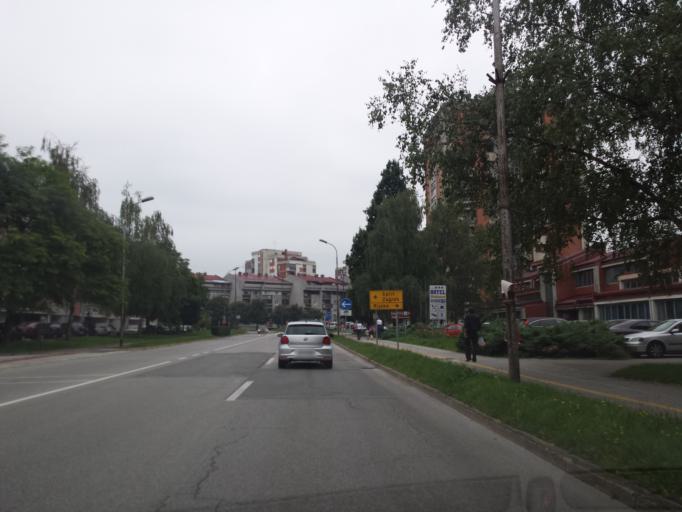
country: HR
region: Karlovacka
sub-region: Grad Karlovac
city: Karlovac
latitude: 45.4865
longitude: 15.5465
